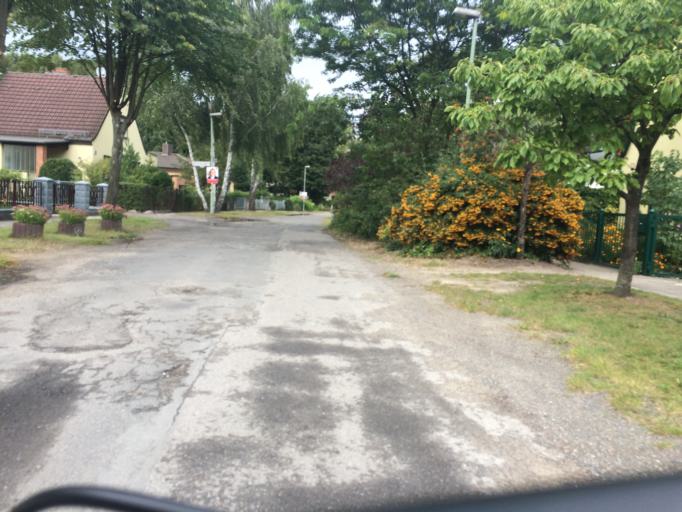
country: DE
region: Berlin
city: Neu-Hohenschoenhausen
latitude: 52.5603
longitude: 13.5051
